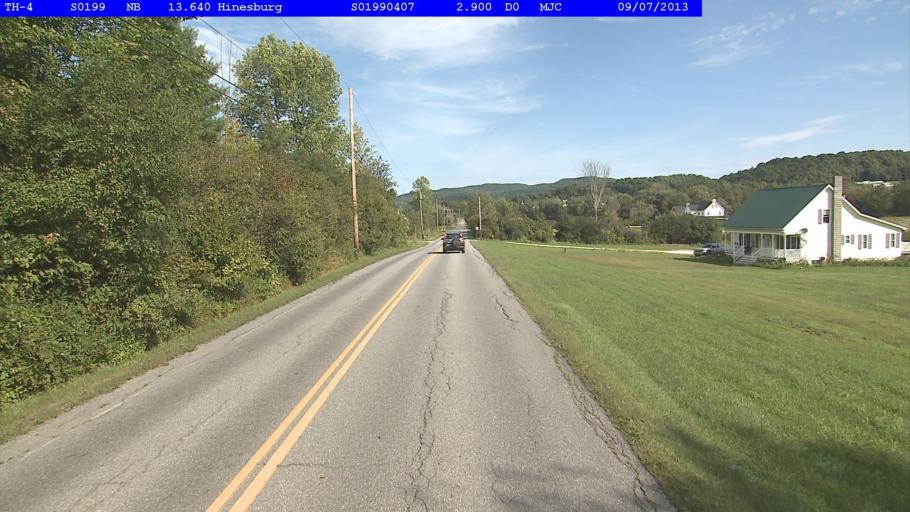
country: US
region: Vermont
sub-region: Chittenden County
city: Hinesburg
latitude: 44.3196
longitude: -73.1100
